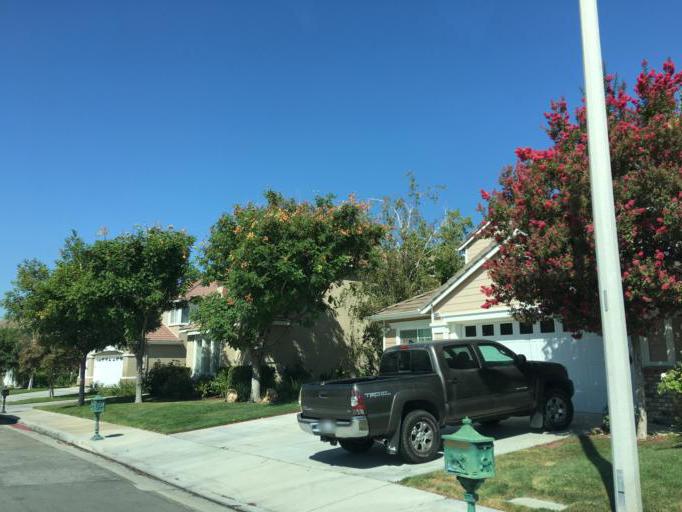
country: US
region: California
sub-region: Los Angeles County
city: Santa Clarita
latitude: 34.3932
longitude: -118.5944
